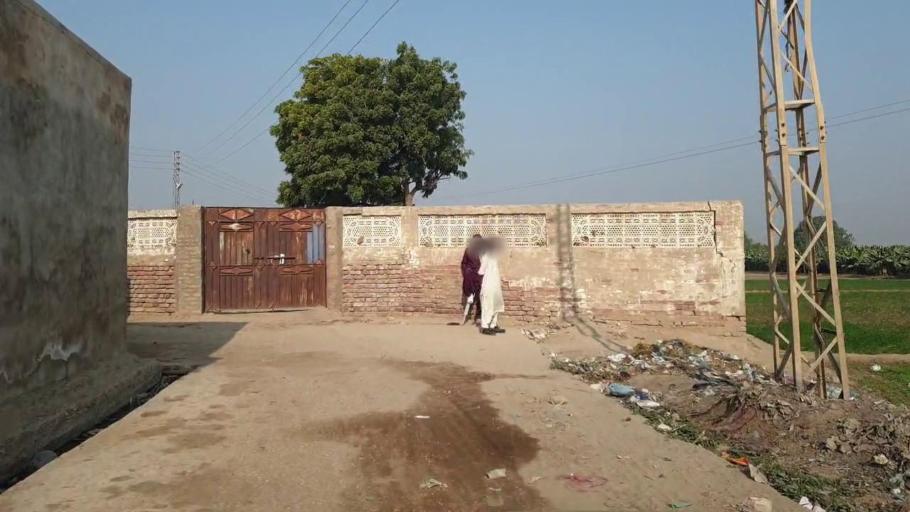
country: PK
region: Sindh
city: Kotri
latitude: 25.3484
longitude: 68.3223
